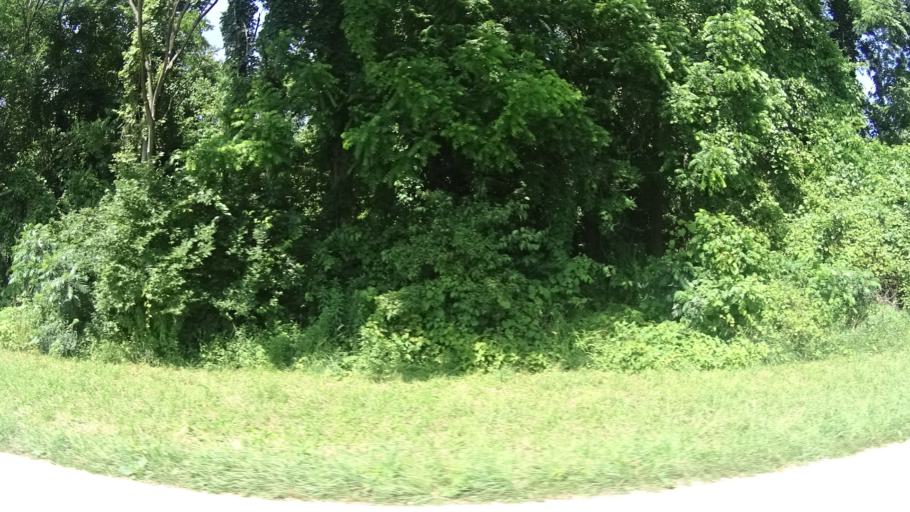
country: US
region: Ohio
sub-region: Erie County
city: Huron
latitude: 41.3497
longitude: -82.4592
